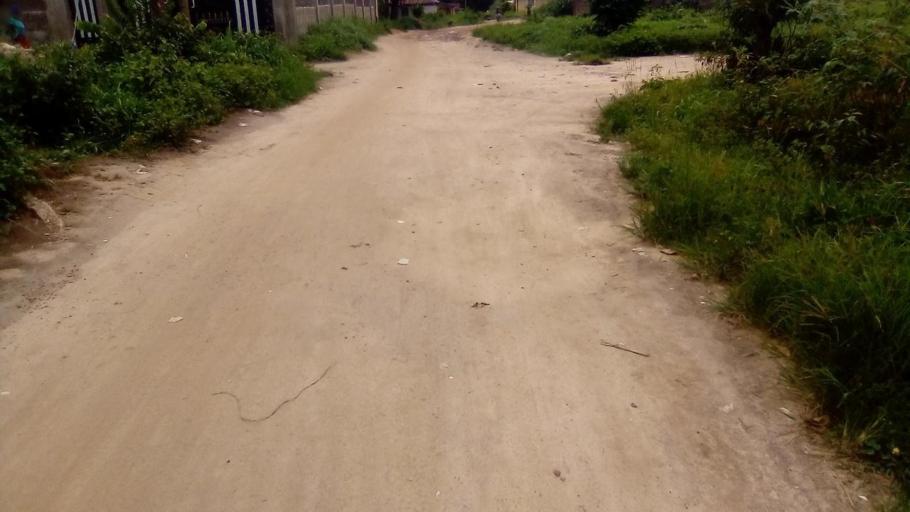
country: SL
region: Southern Province
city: Bo
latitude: 7.9381
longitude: -11.7454
